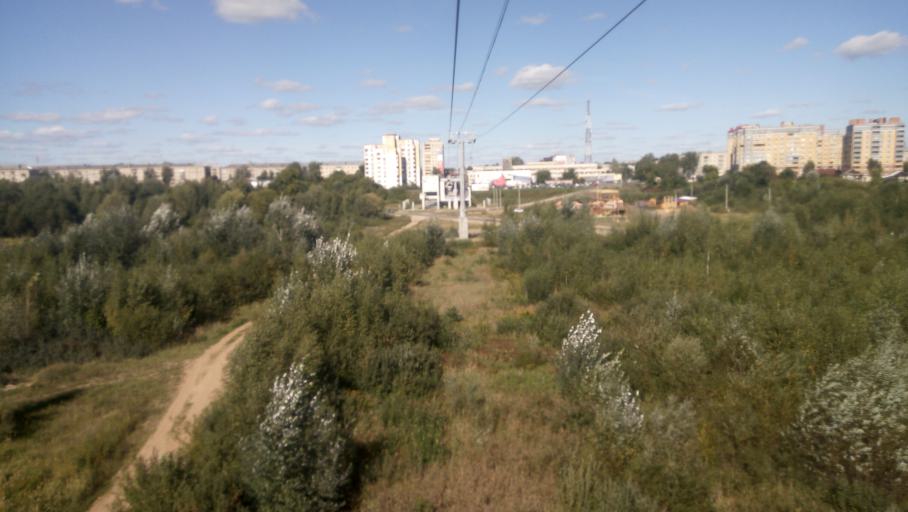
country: RU
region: Nizjnij Novgorod
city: Bor
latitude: 56.3514
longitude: 44.0592
